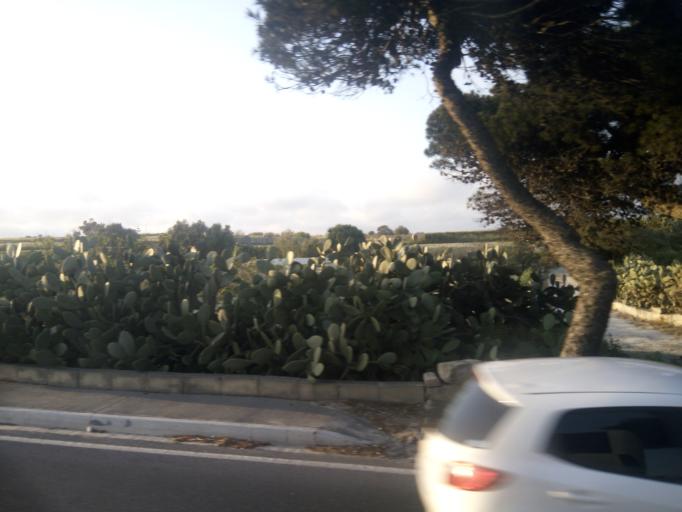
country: MT
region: L-Imdina
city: Imdina
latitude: 35.8835
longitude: 14.4159
